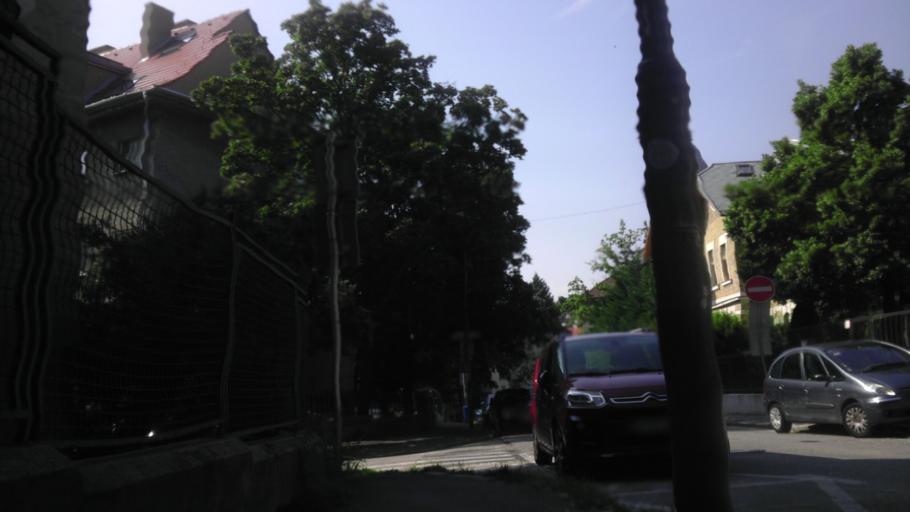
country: SK
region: Bratislavsky
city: Bratislava
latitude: 48.1518
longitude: 17.1048
